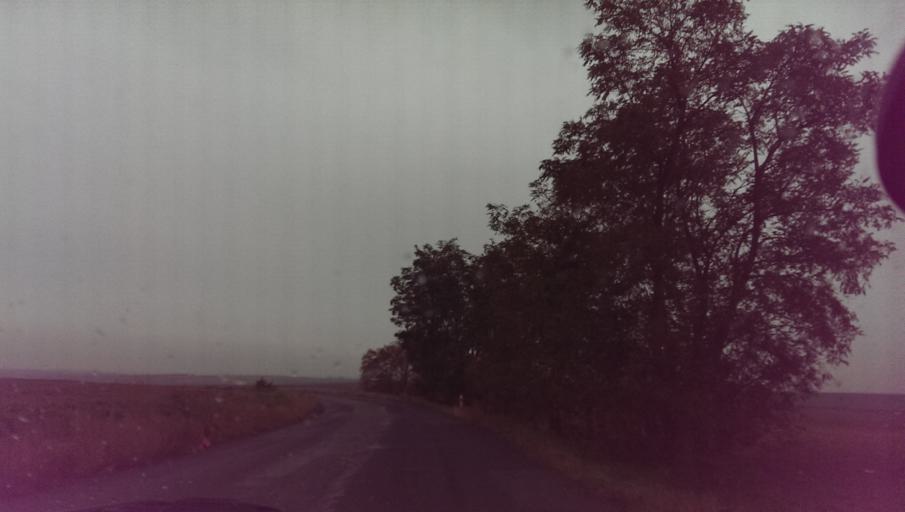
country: CZ
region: South Moravian
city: Orechov
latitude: 49.0933
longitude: 16.5268
